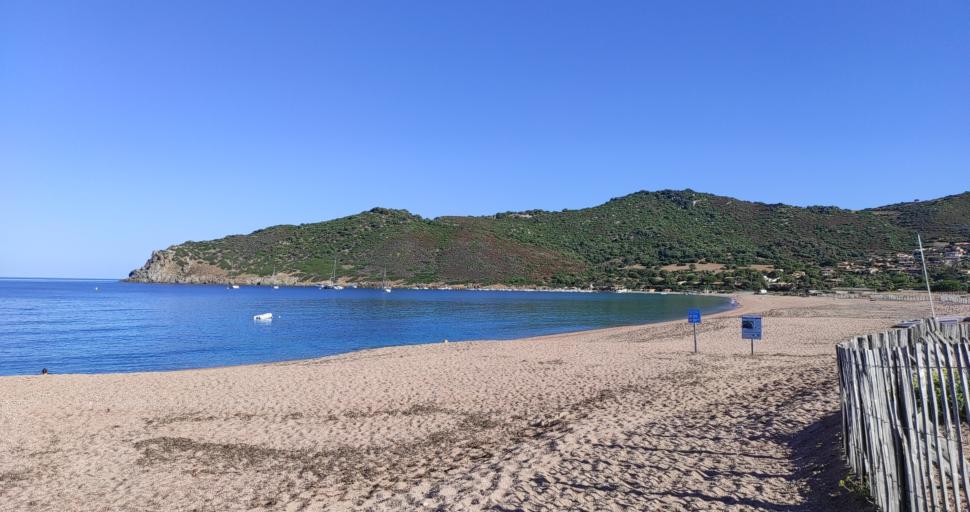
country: FR
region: Corsica
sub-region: Departement de la Corse-du-Sud
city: Alata
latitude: 41.9867
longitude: 8.6704
